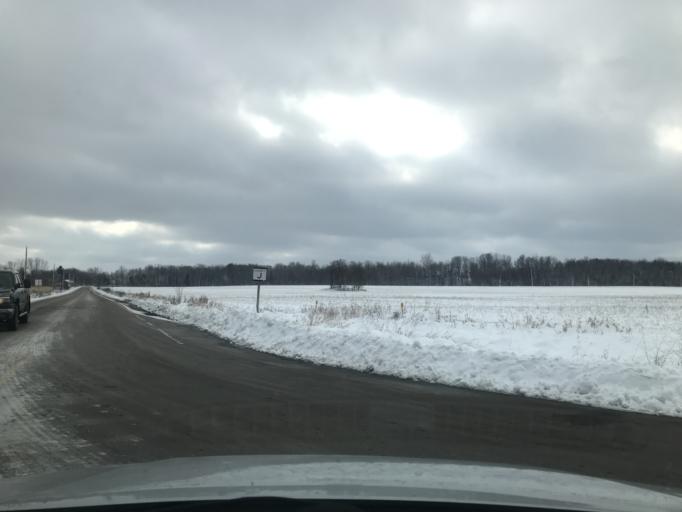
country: US
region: Wisconsin
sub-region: Oconto County
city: Oconto
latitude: 44.9504
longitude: -87.9873
